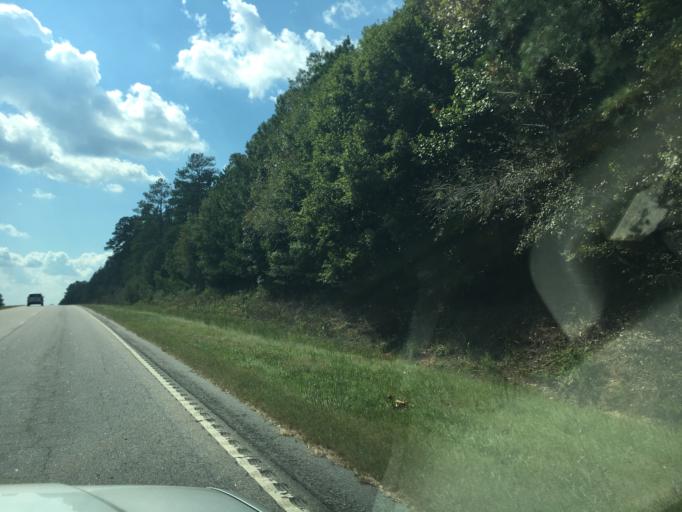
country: US
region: South Carolina
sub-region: Pickens County
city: Liberty
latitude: 34.7576
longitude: -82.6943
